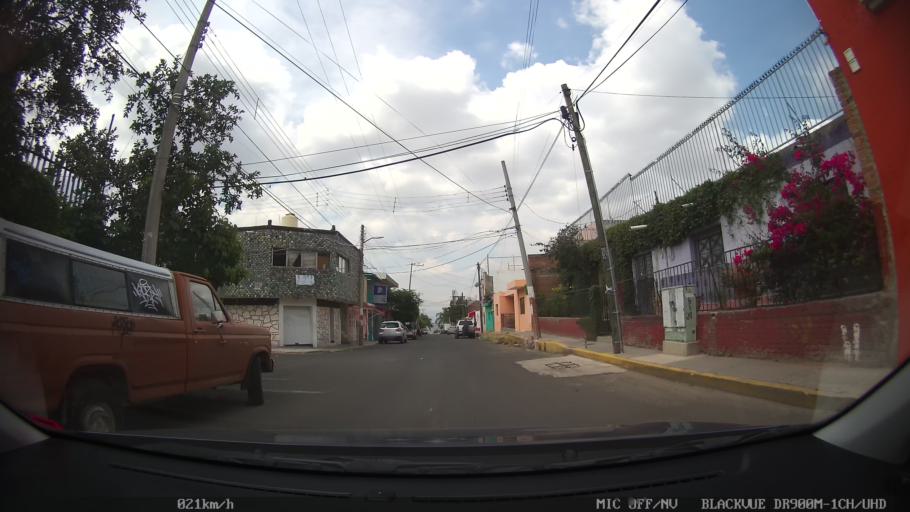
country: MX
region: Jalisco
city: Tonala
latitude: 20.6186
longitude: -103.2428
